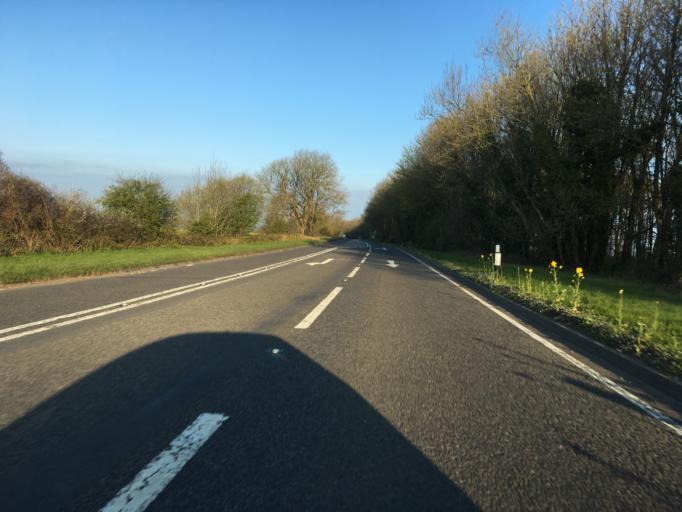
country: GB
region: England
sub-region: Gloucestershire
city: Shipton Village
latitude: 51.8585
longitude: -1.9029
